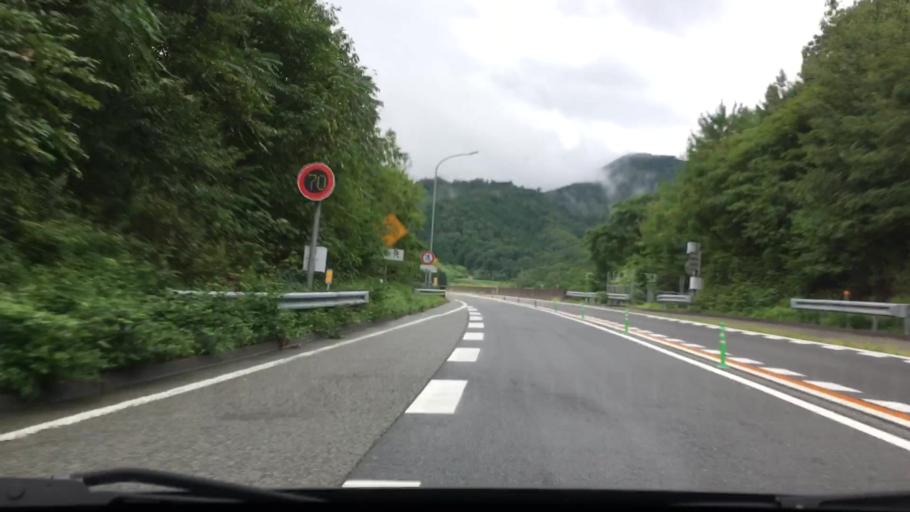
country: JP
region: Hyogo
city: Toyooka
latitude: 35.3112
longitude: 134.8281
